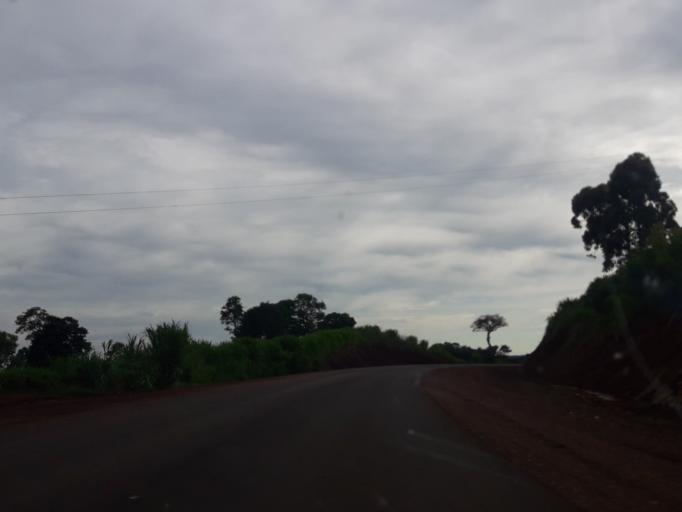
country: AR
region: Misiones
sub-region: Departamento de San Pedro
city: San Pedro
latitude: -26.5092
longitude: -53.9223
